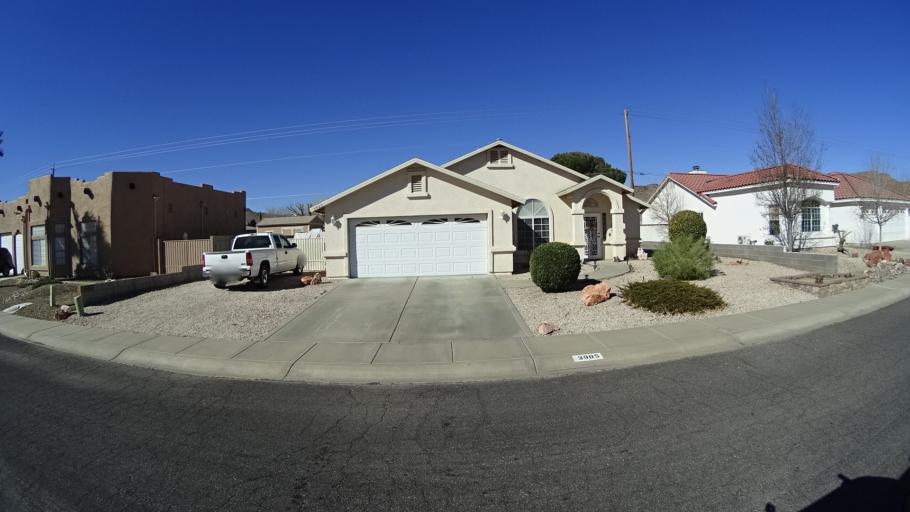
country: US
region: Arizona
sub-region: Mohave County
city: New Kingman-Butler
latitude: 35.2351
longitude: -114.0397
